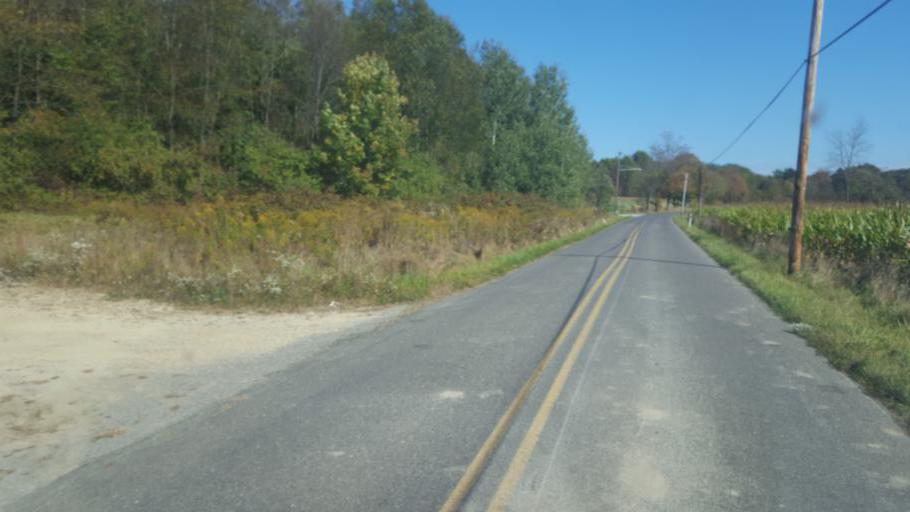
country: US
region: Pennsylvania
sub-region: Mercer County
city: Reynolds Heights
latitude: 41.3673
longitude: -80.3680
